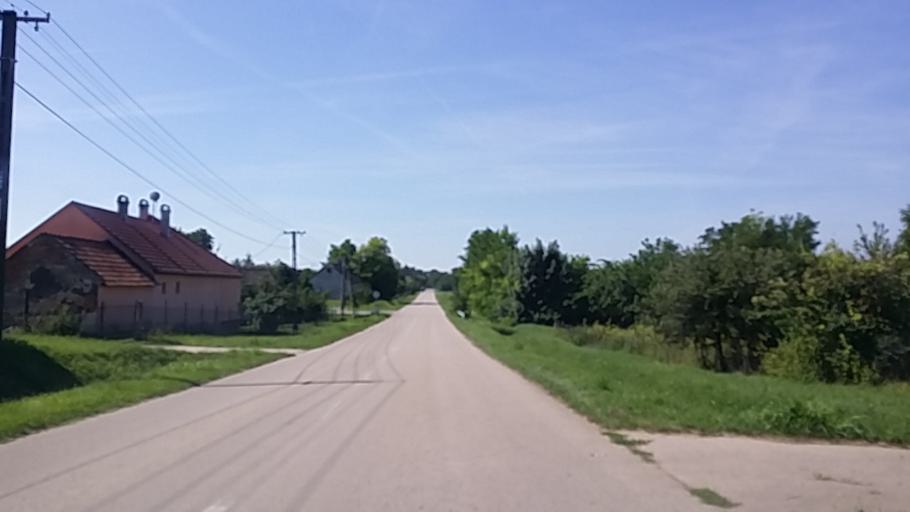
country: HU
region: Fejer
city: Deg
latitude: 46.8791
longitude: 18.4455
